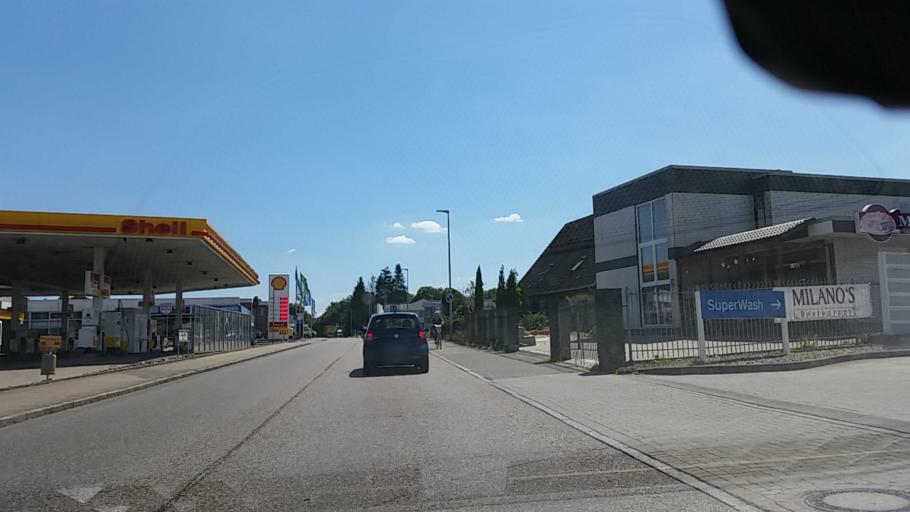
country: DE
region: Schleswig-Holstein
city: Kaltenkirchen
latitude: 53.8408
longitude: 9.9481
